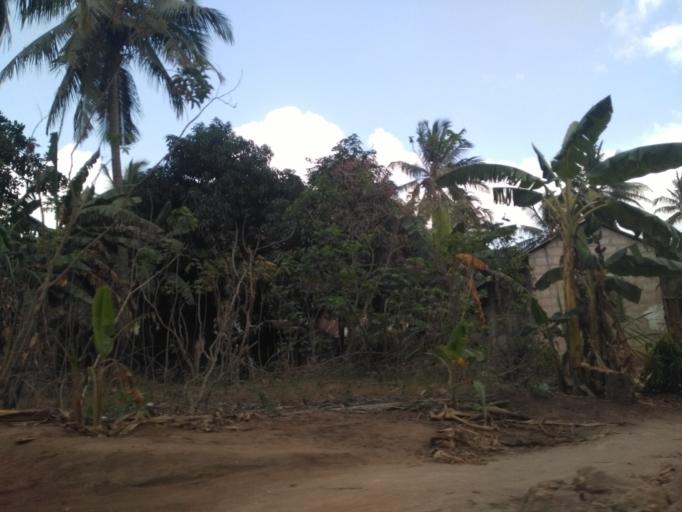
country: TZ
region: Dar es Salaam
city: Dar es Salaam
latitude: -6.8837
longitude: 39.3365
